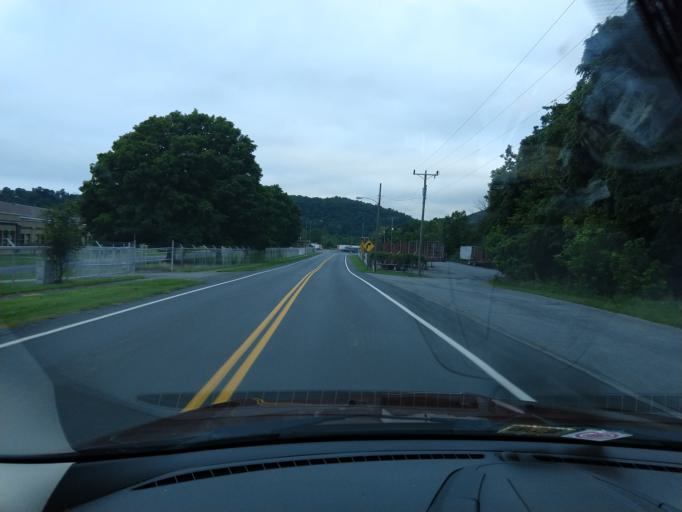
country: US
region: Virginia
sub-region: City of Covington
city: Fairlawn
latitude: 37.7607
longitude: -79.9988
